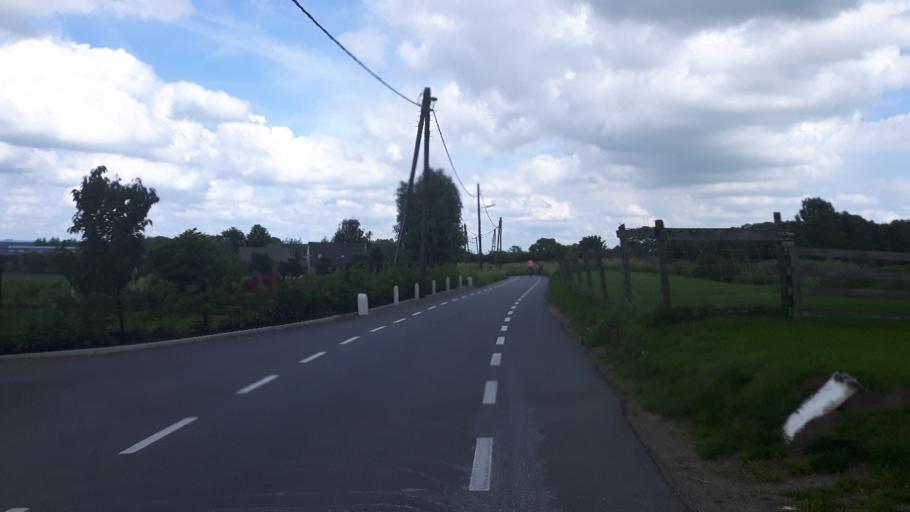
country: NL
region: Utrecht
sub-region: Gemeente Oudewater
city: Oudewater
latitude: 52.0203
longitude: 4.8504
